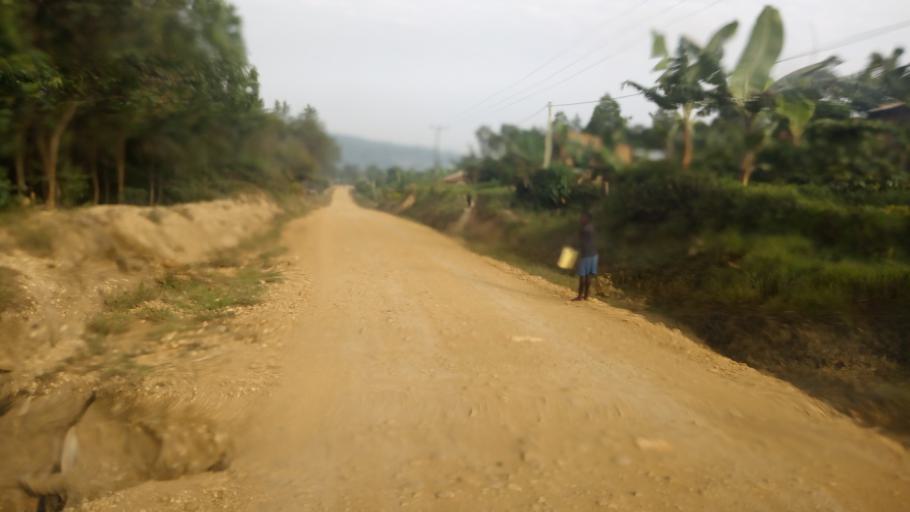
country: UG
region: Western Region
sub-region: Kanungu District
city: Ntungamo
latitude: -0.8397
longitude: 29.6523
